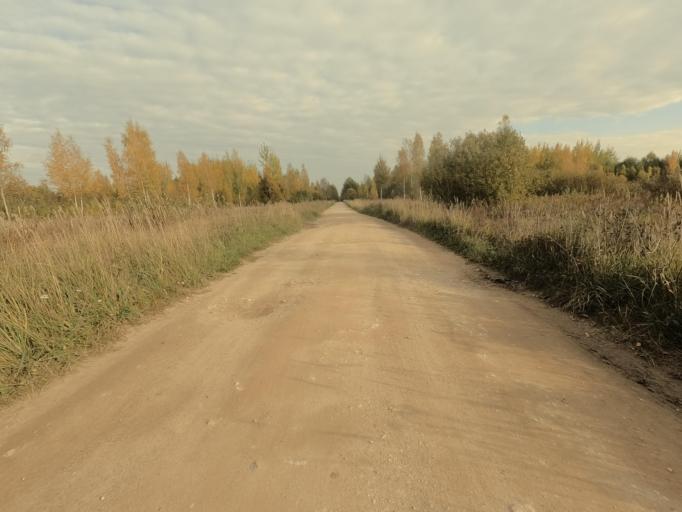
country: RU
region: Novgorod
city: Pankovka
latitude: 58.8964
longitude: 31.0040
